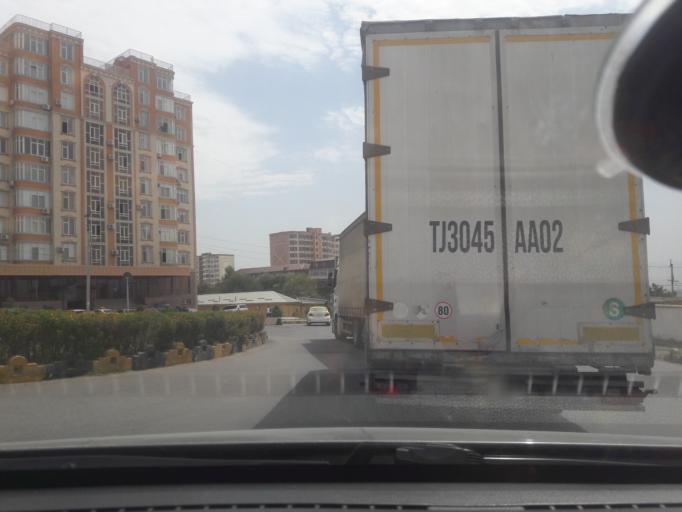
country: TJ
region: Dushanbe
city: Dushanbe
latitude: 38.5828
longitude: 68.7059
